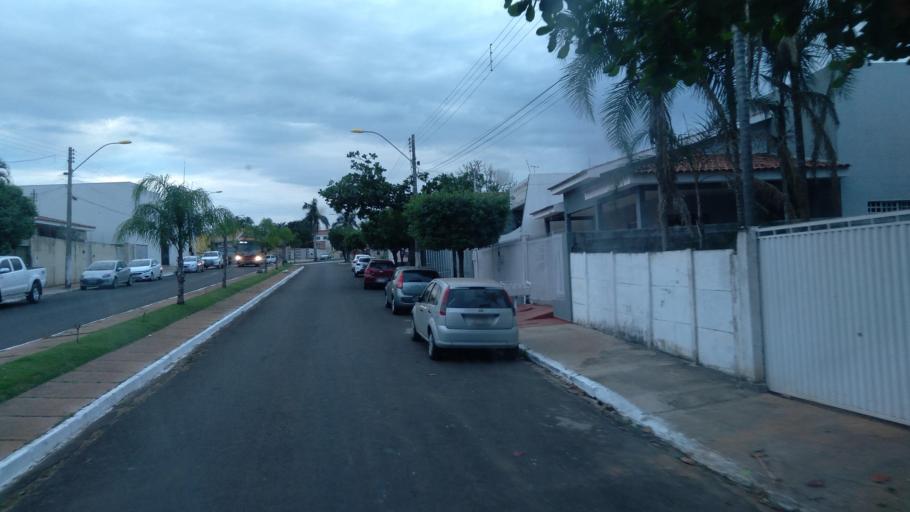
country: BR
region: Goias
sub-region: Mineiros
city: Mineiros
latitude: -17.5685
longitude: -52.5503
